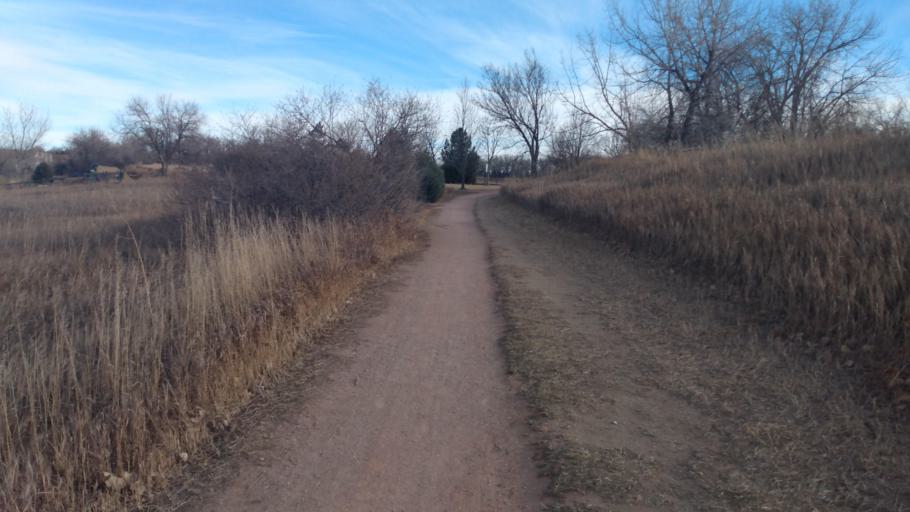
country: US
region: Colorado
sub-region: Boulder County
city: Gunbarrel
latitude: 40.0639
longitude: -105.2015
